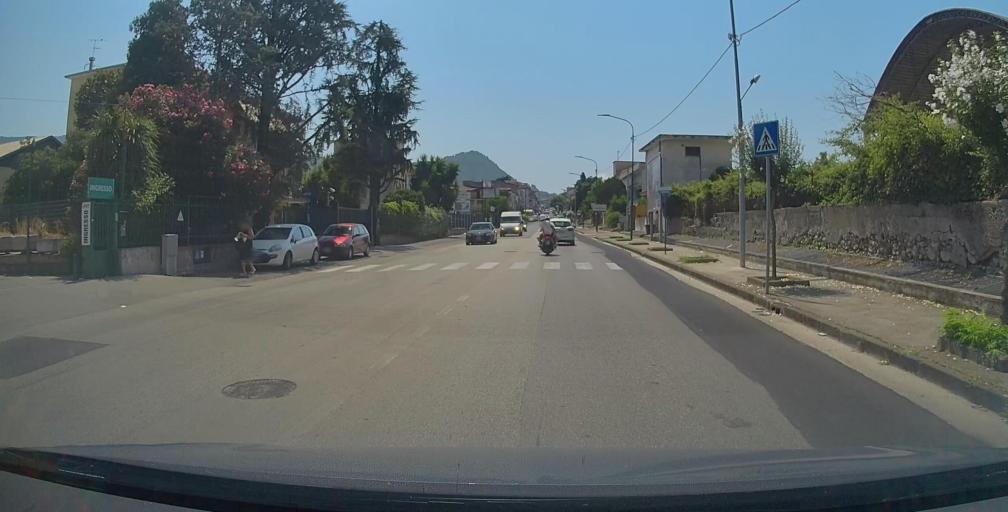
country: IT
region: Campania
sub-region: Provincia di Salerno
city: Nocera Superiore
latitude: 40.7244
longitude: 14.6939
